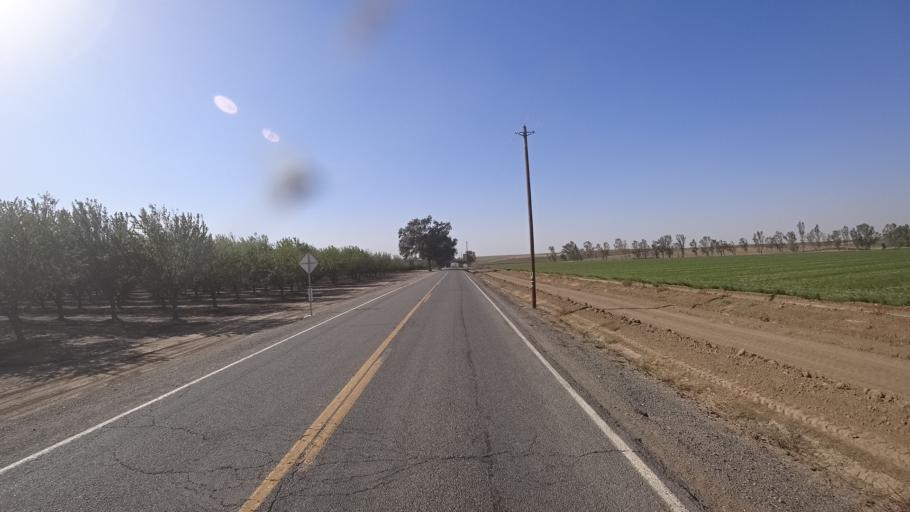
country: US
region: California
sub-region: Yolo County
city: Woodland
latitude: 38.7058
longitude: -121.8632
